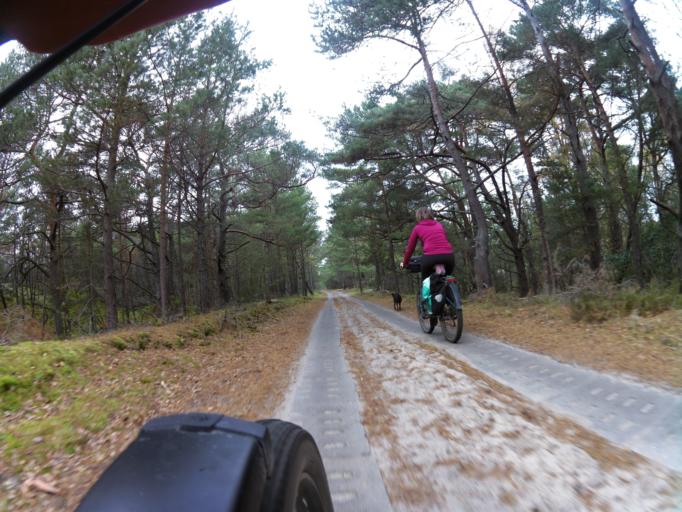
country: PL
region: Pomeranian Voivodeship
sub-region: Powiat pucki
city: Hel
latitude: 54.6289
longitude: 18.8126
